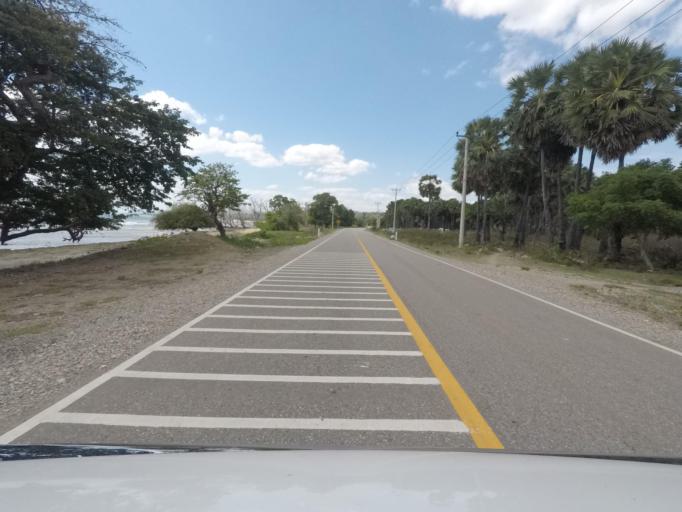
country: TL
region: Lautem
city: Lospalos
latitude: -8.4216
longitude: 126.7615
